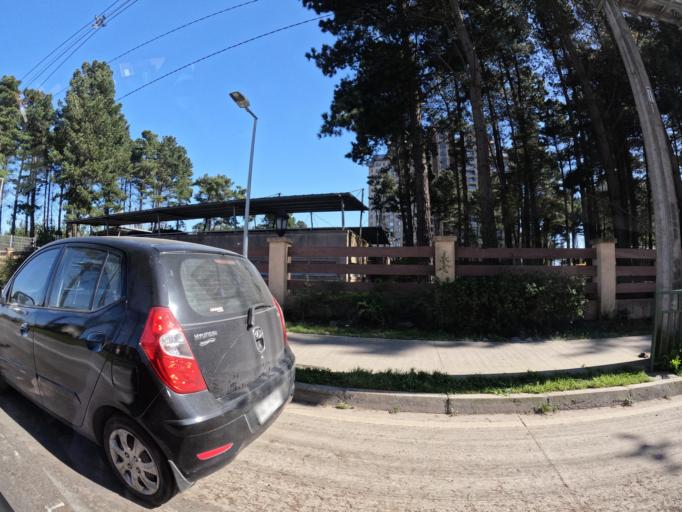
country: CL
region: Biobio
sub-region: Provincia de Concepcion
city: Concepcion
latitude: -36.8859
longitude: -73.1496
